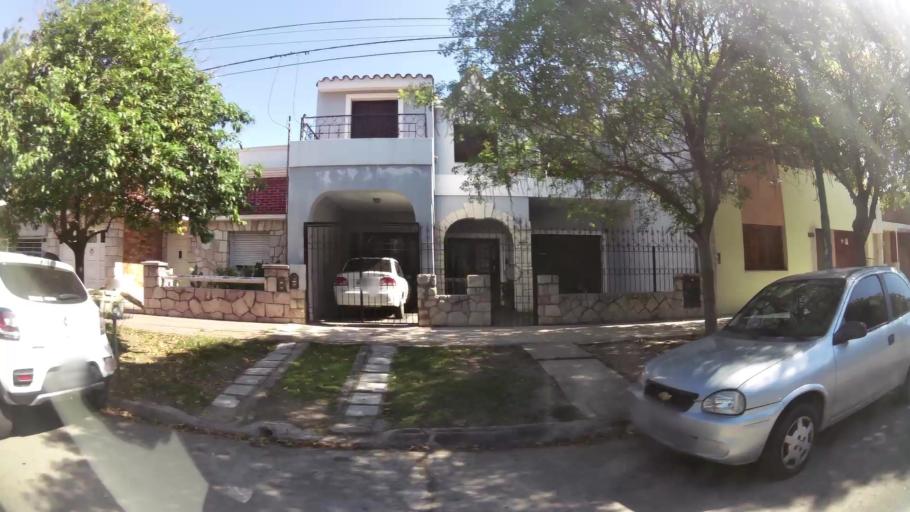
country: AR
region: Cordoba
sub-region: Departamento de Capital
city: Cordoba
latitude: -31.4195
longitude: -64.1666
